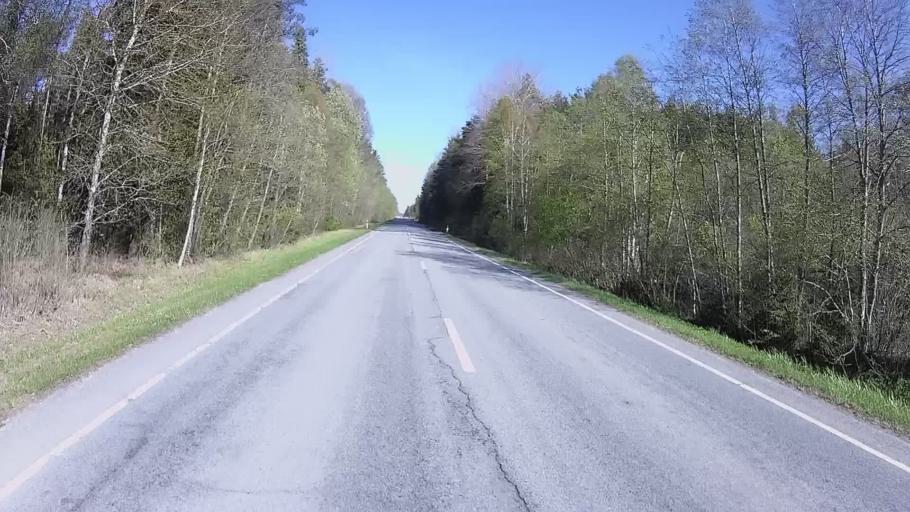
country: EE
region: Raplamaa
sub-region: Jaervakandi vald
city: Jarvakandi
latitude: 58.8501
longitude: 24.7950
